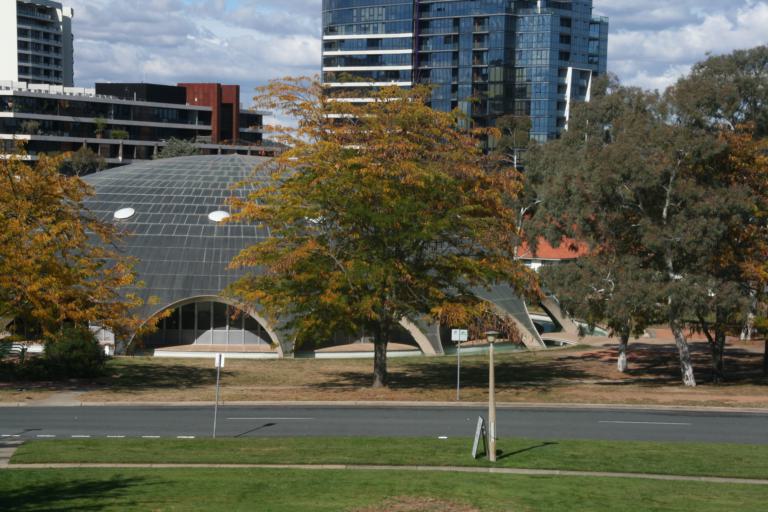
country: AU
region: Australian Capital Territory
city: Canberra
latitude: -35.2837
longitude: 149.1227
